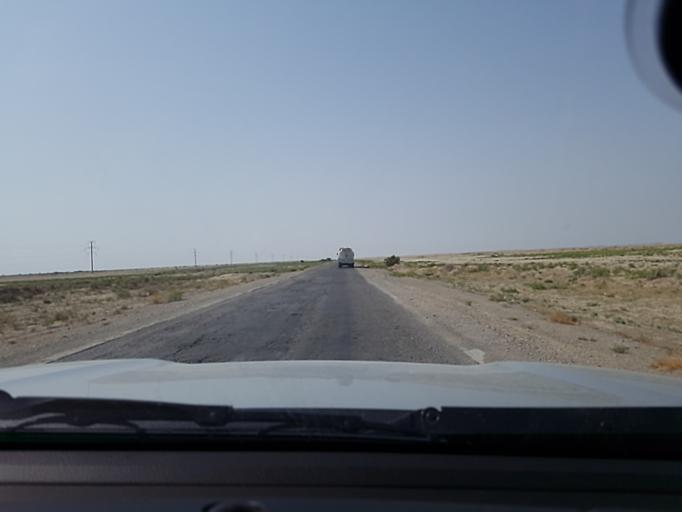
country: TM
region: Balkan
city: Gumdag
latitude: 38.8612
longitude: 54.5947
